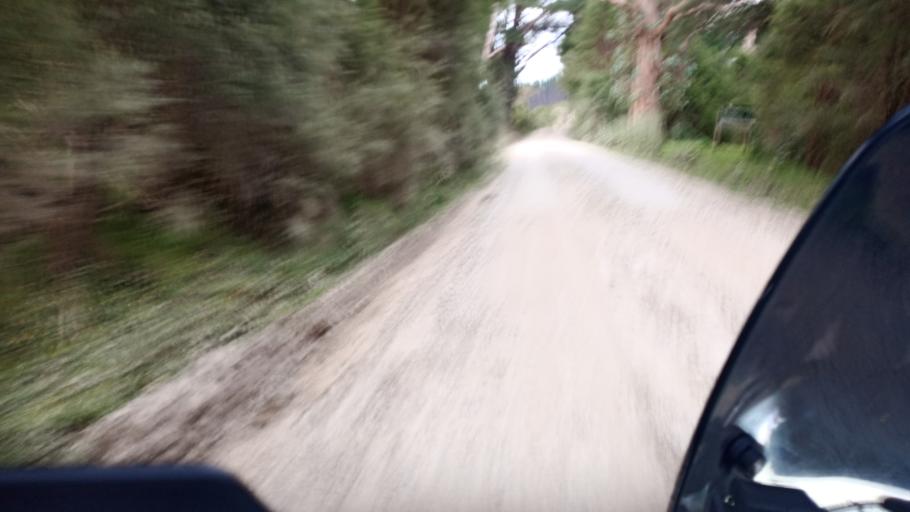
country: NZ
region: Gisborne
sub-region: Gisborne District
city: Gisborne
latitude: -38.4695
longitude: 177.9763
